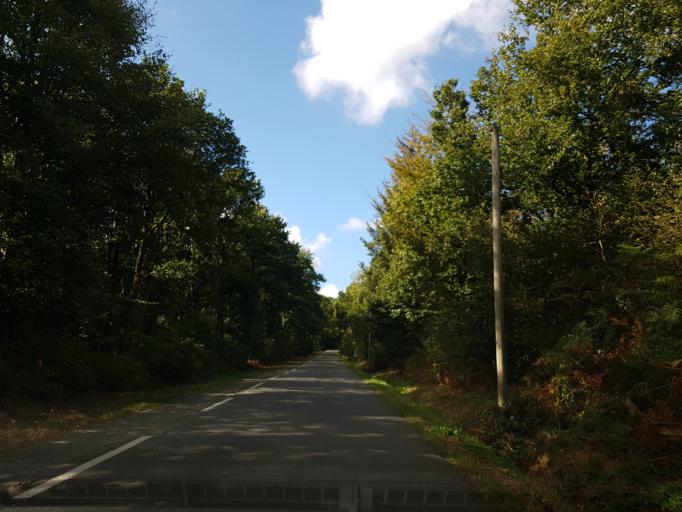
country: FR
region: Brittany
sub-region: Departement des Cotes-d'Armor
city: Pledran
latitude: 48.4590
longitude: -2.7228
